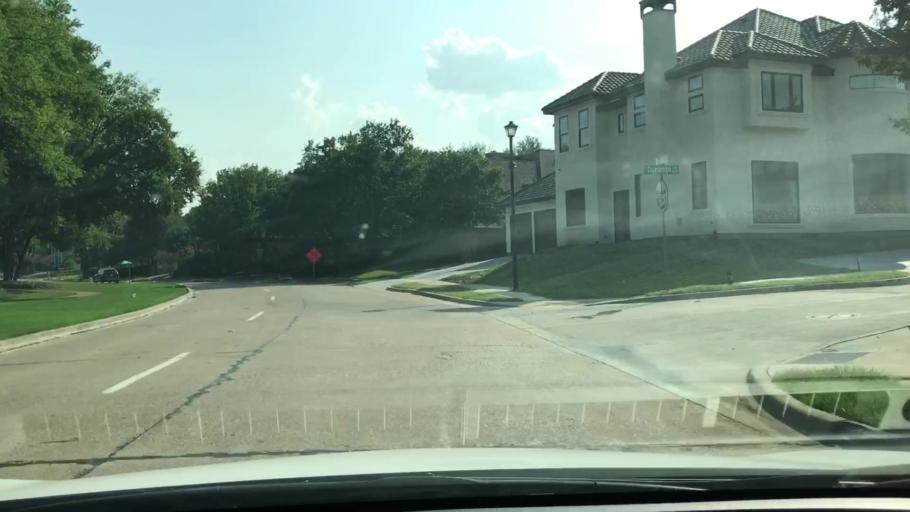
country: US
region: Texas
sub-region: Dallas County
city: Irving
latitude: 32.8508
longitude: -96.9353
